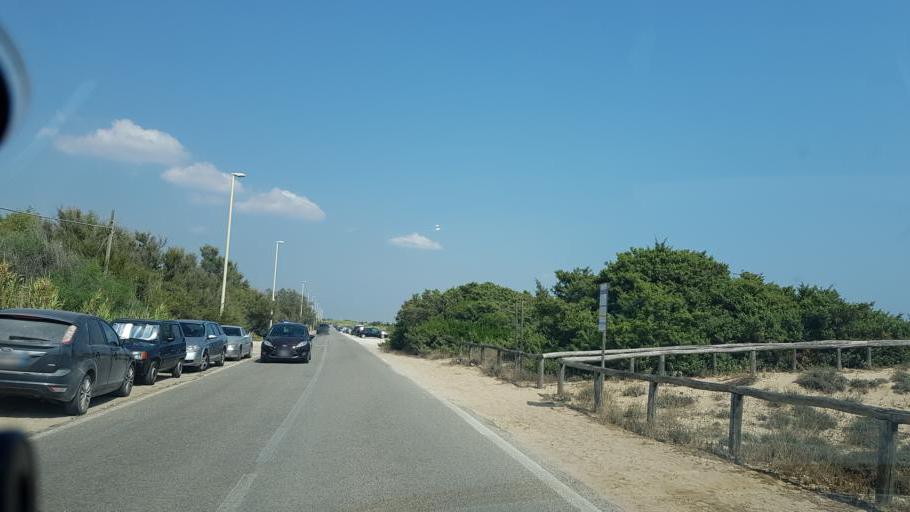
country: IT
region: Apulia
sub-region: Provincia di Taranto
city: Maruggio
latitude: 40.3026
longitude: 17.6266
